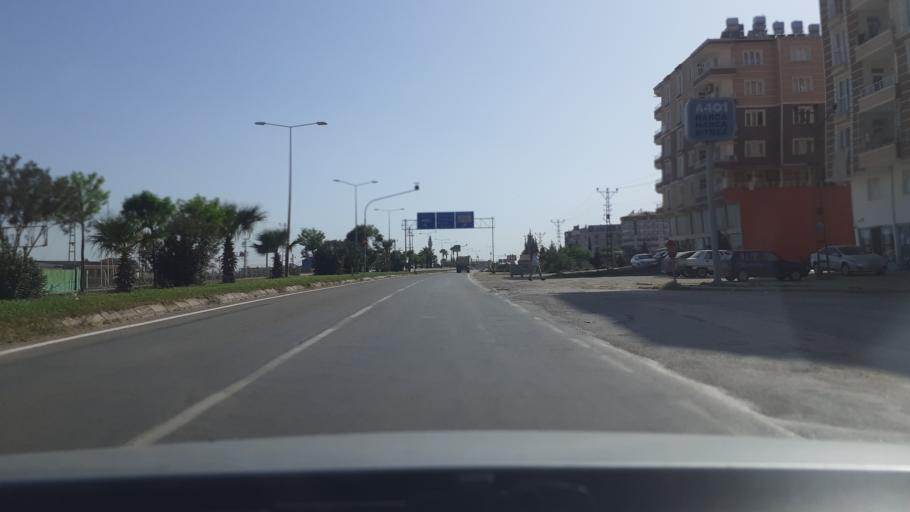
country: TR
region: Hatay
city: Kirikhan
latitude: 36.4898
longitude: 36.3685
